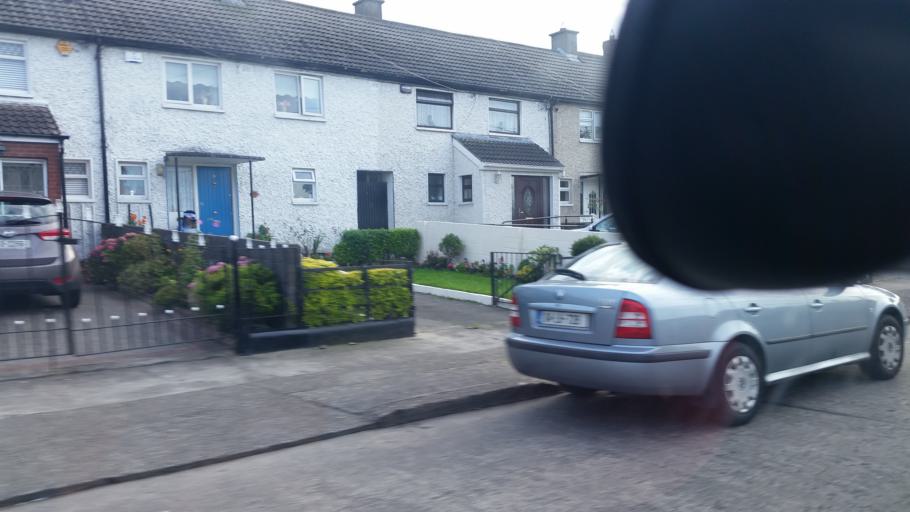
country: IE
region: Leinster
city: Beaumont
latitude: 53.3958
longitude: -6.2329
